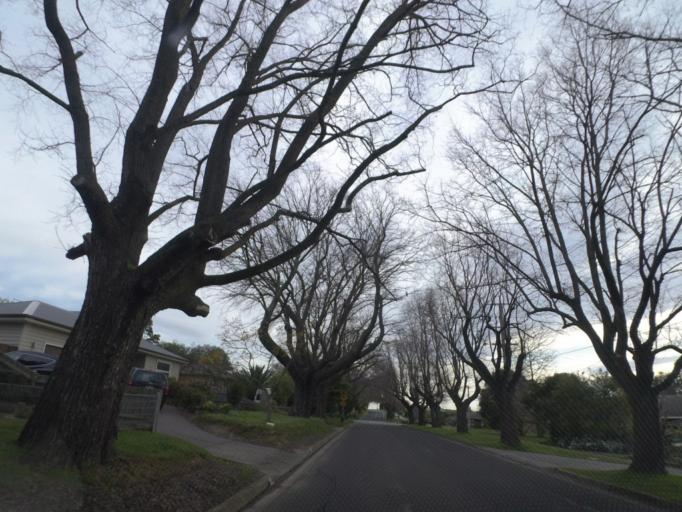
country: AU
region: Victoria
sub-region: Knox
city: Ferntree Gully
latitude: -37.8930
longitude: 145.2861
